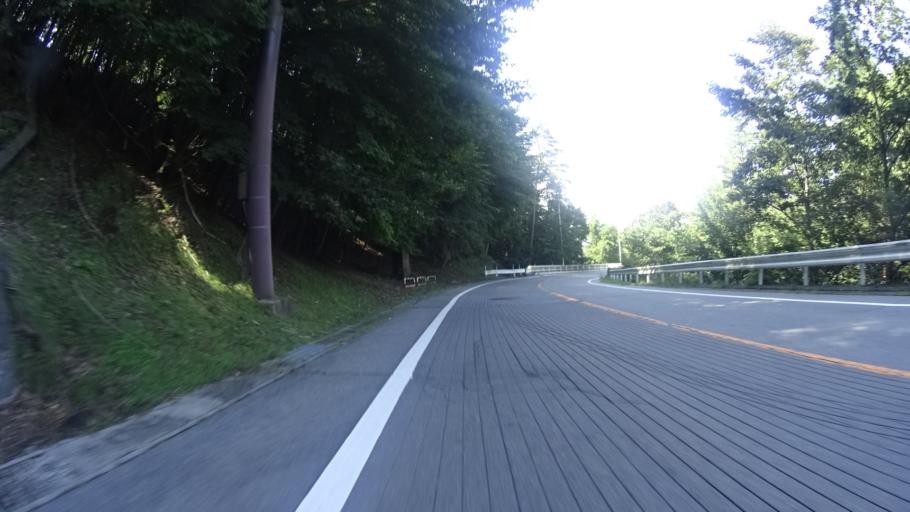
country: JP
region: Yamanashi
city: Enzan
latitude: 35.7508
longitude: 138.8102
